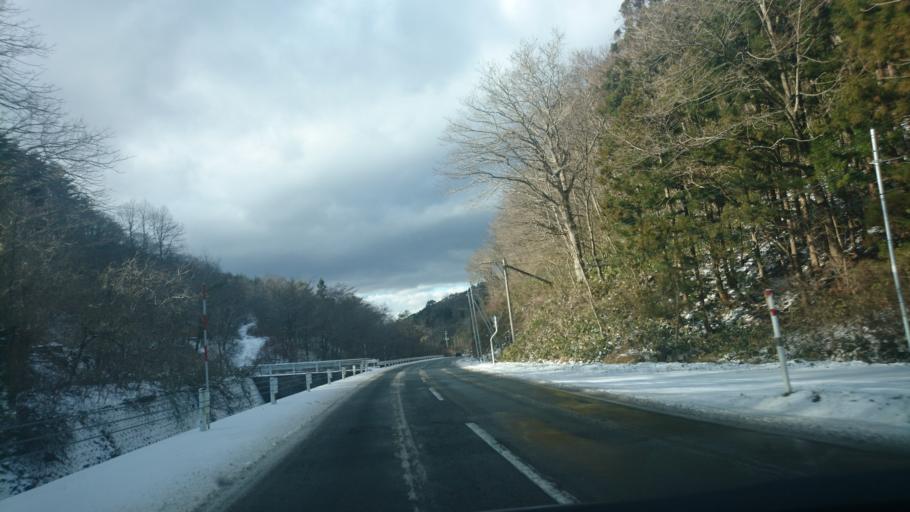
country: JP
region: Iwate
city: Tono
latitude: 39.1682
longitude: 141.3594
